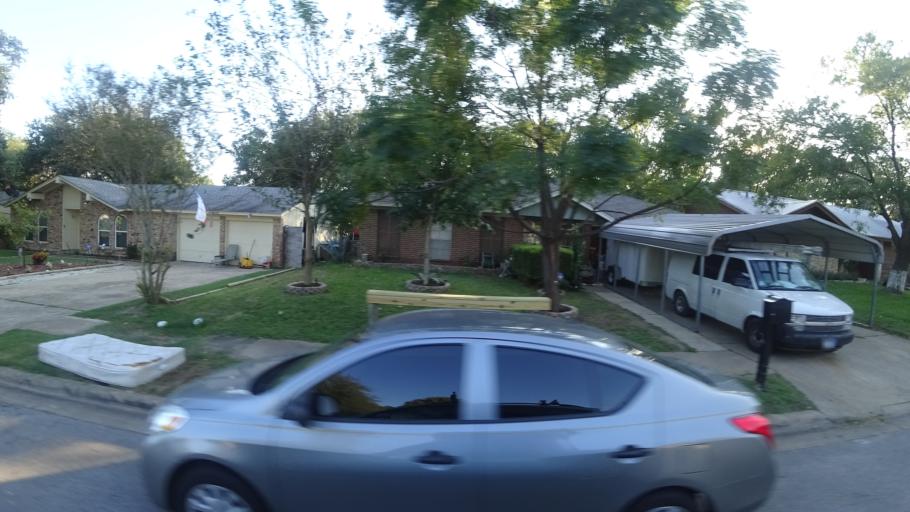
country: US
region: Texas
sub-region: Travis County
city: Wells Branch
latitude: 30.3594
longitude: -97.6766
